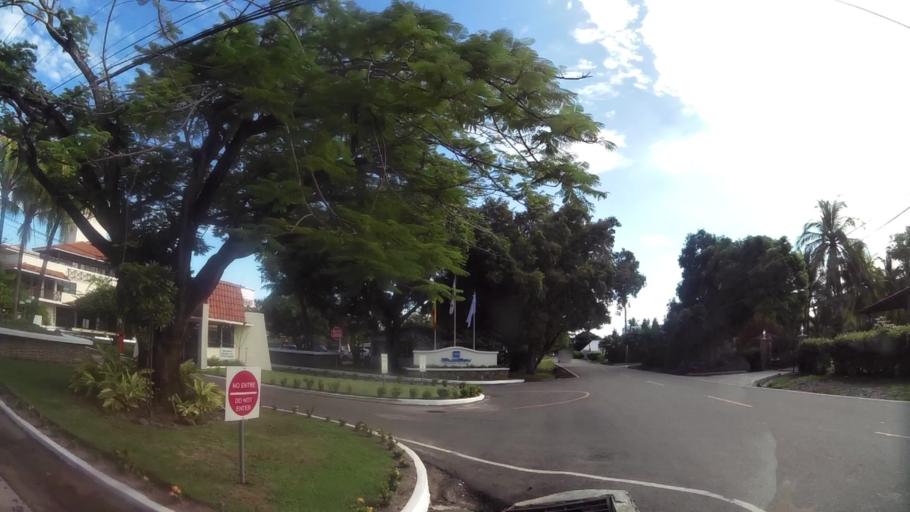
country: PA
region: Panama
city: Nueva Gorgona
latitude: 8.5329
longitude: -79.8846
